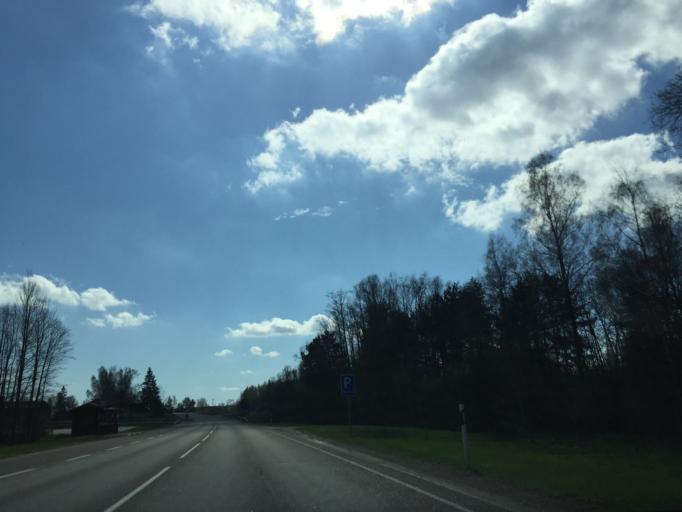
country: EE
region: Valgamaa
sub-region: Torva linn
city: Torva
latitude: 58.0573
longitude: 26.1949
